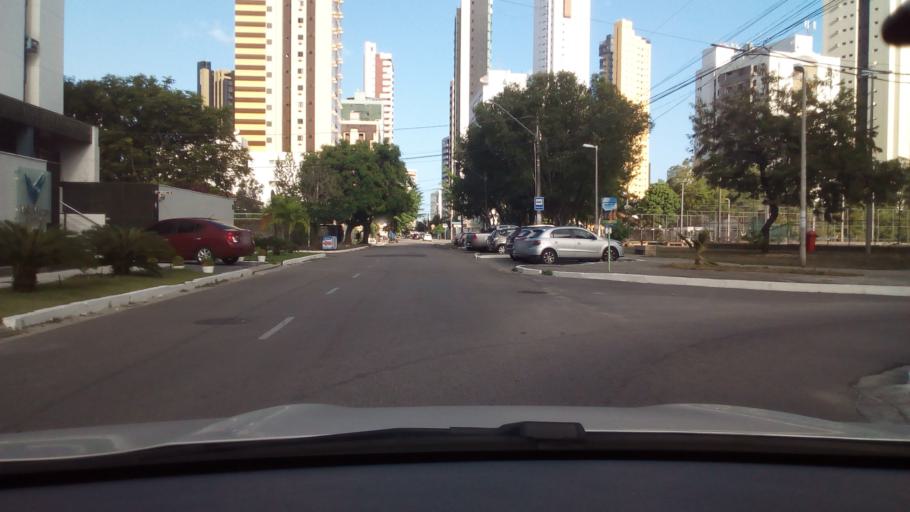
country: BR
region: Paraiba
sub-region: Joao Pessoa
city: Joao Pessoa
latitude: -7.0997
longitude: -34.8411
